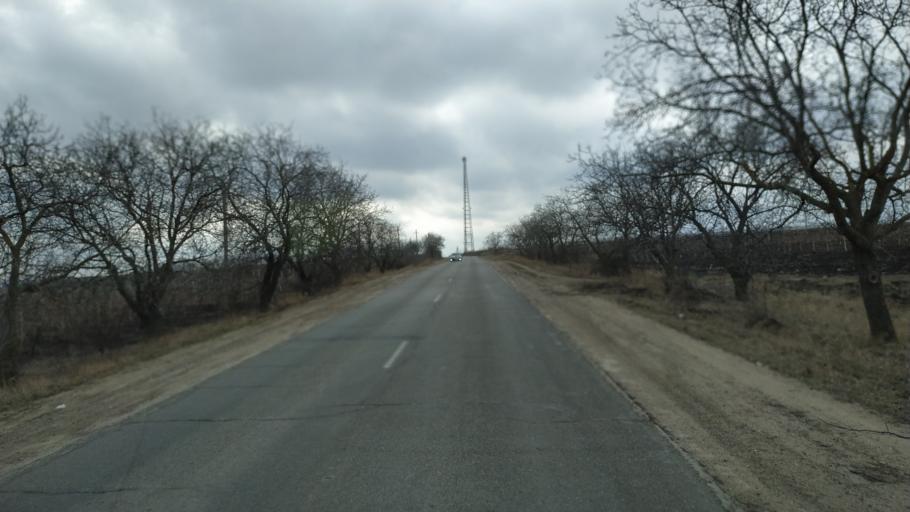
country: MD
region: Laloveni
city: Ialoveni
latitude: 46.8914
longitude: 28.7692
